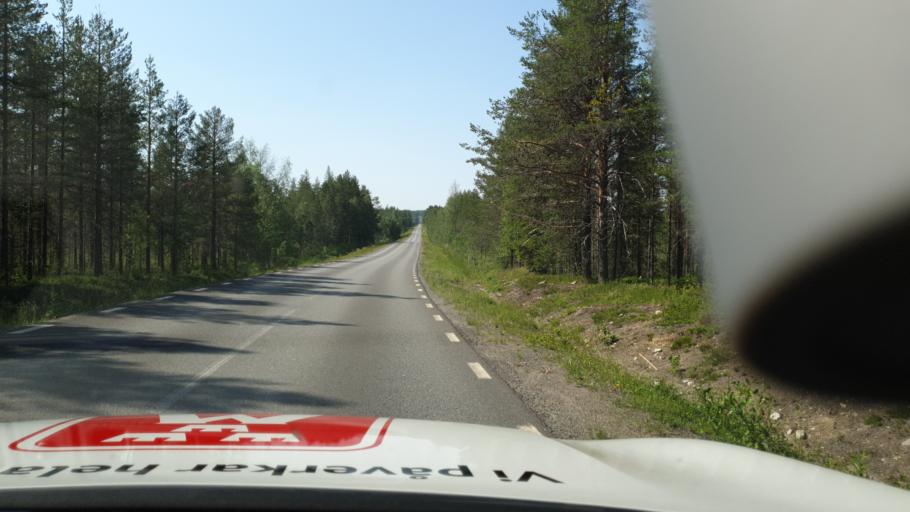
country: SE
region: Vaesterbotten
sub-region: Skelleftea Kommun
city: Langsele
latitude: 64.9894
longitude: 20.0845
